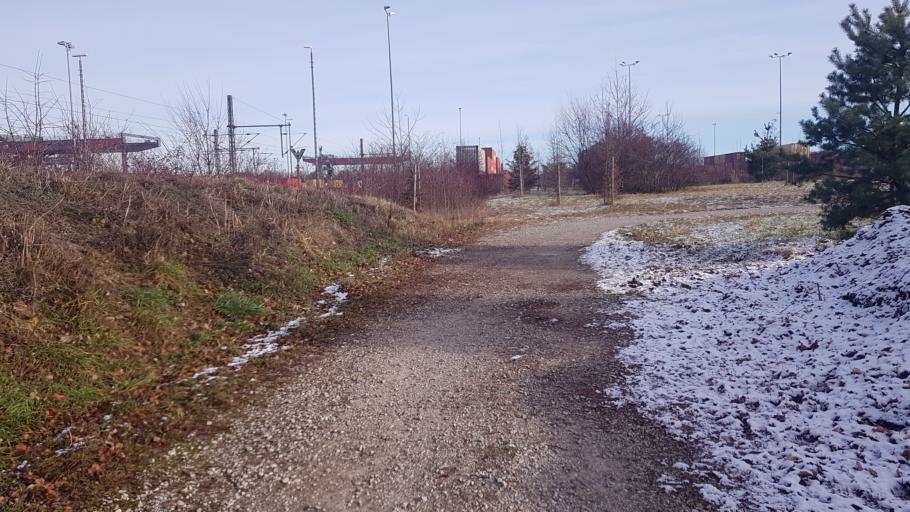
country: DE
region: Bavaria
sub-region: Upper Bavaria
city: Feldkirchen
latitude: 48.1446
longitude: 11.7002
